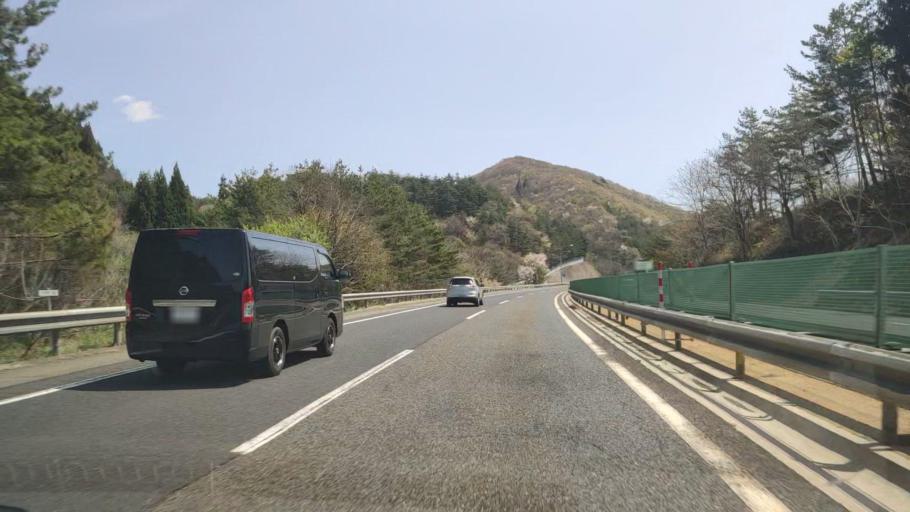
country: JP
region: Iwate
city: Ichinohe
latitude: 40.2323
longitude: 141.2959
